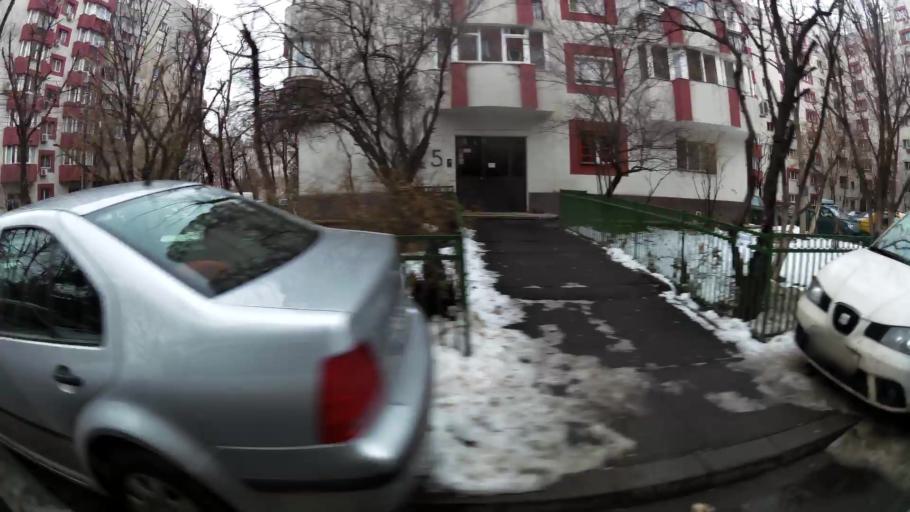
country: RO
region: Bucuresti
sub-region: Municipiul Bucuresti
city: Bucuresti
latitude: 44.4151
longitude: 26.0649
